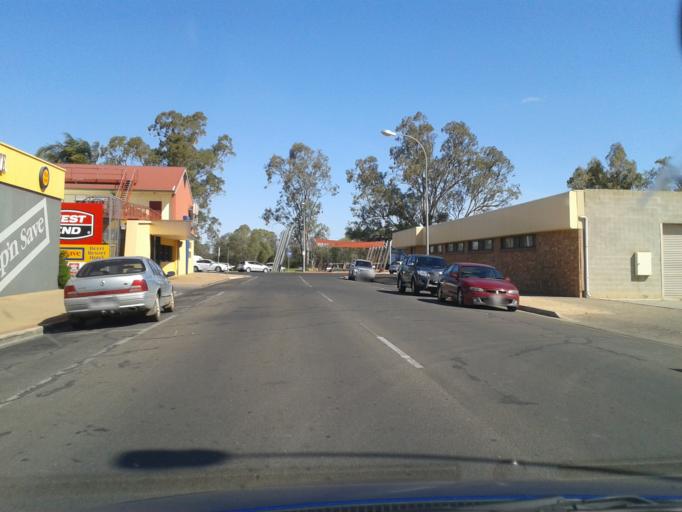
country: AU
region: South Australia
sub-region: Berri and Barmera
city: Berri
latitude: -34.2868
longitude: 140.6035
